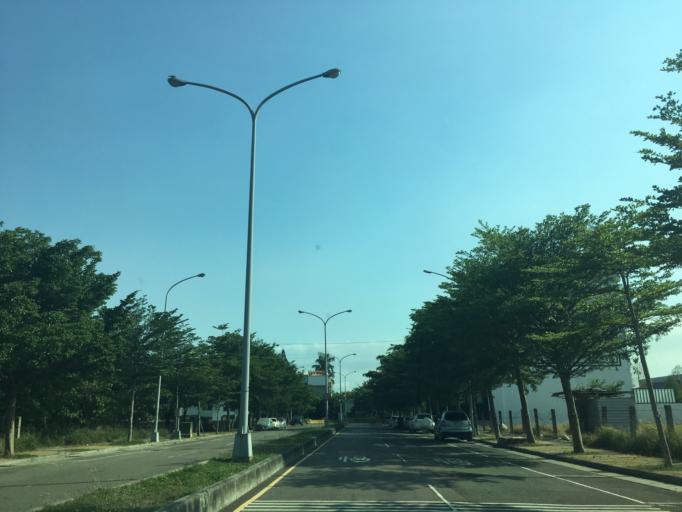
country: TW
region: Taiwan
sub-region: Taichung City
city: Taichung
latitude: 24.1555
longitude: 120.6279
